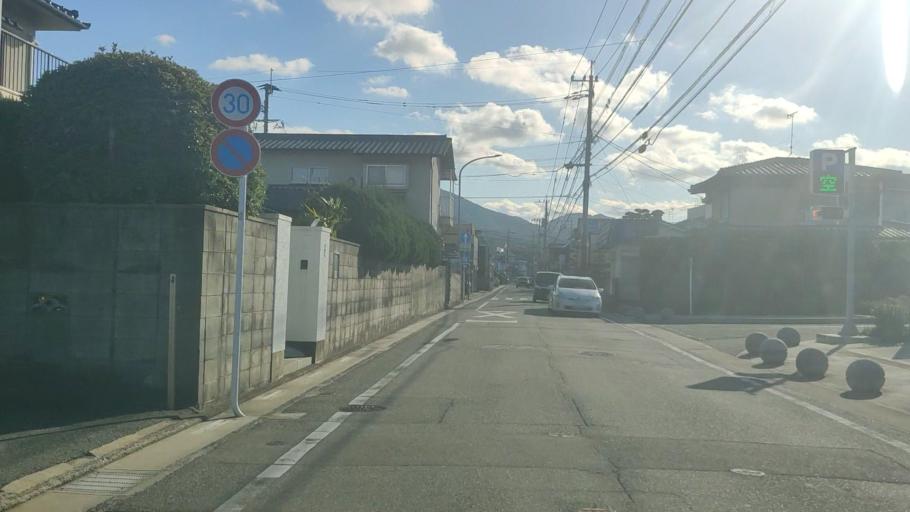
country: JP
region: Fukuoka
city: Fukuoka-shi
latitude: 33.5522
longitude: 130.3576
